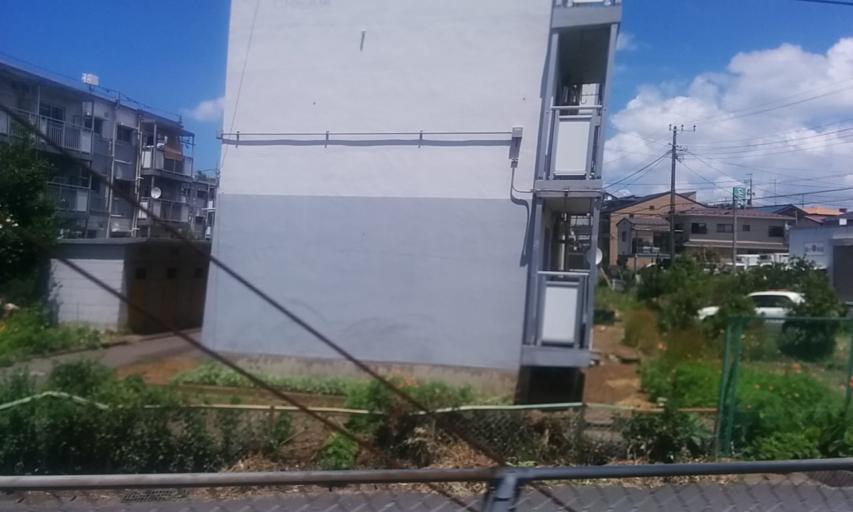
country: JP
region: Chiba
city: Chiba
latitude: 35.5755
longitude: 140.1365
